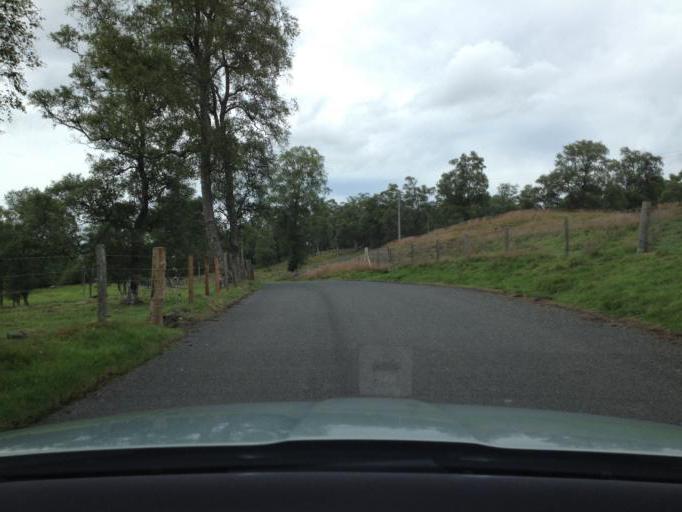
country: GB
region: Scotland
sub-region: Aberdeenshire
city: Aboyne
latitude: 56.8991
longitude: -2.8101
